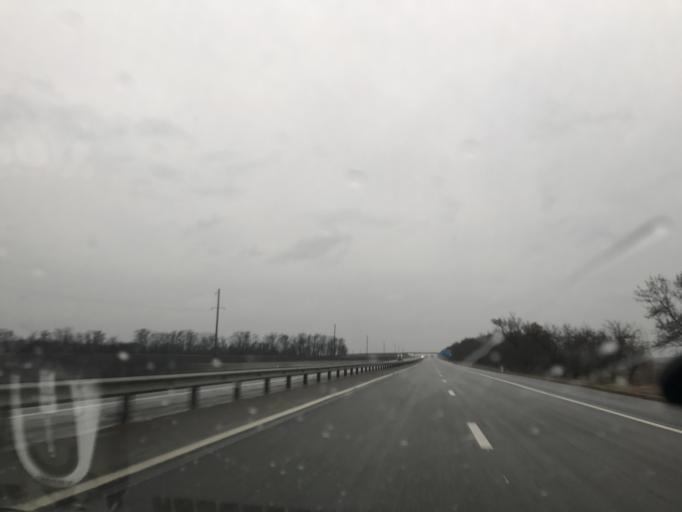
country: RU
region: Krasnodarskiy
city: Kislyakovskaya
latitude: 46.3976
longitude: 39.7316
